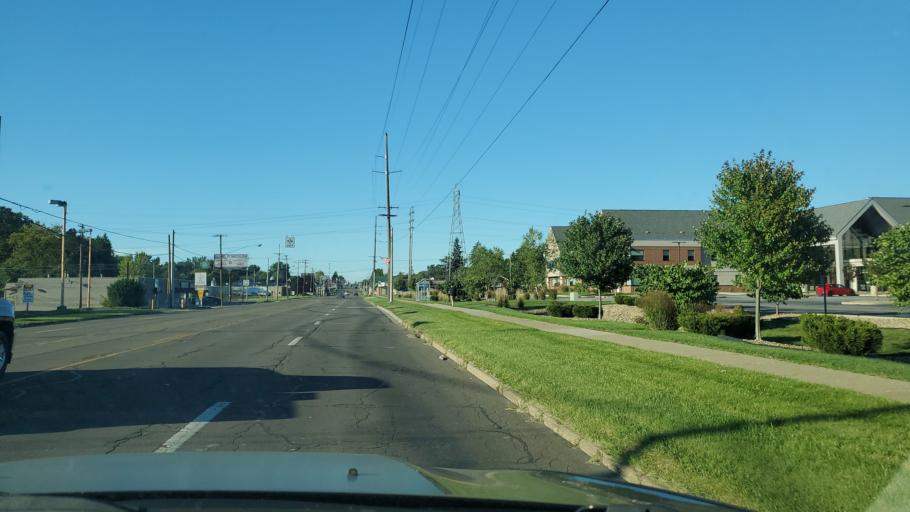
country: US
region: Ohio
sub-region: Mahoning County
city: Boardman
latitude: 41.0302
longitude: -80.6624
